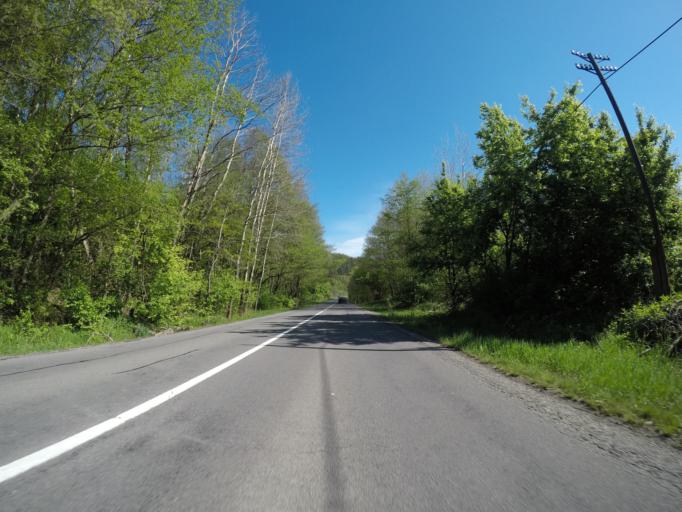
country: SK
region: Banskobystricky
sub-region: Okres Banska Bystrica
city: Banska Stiavnica
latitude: 48.4844
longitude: 18.9444
